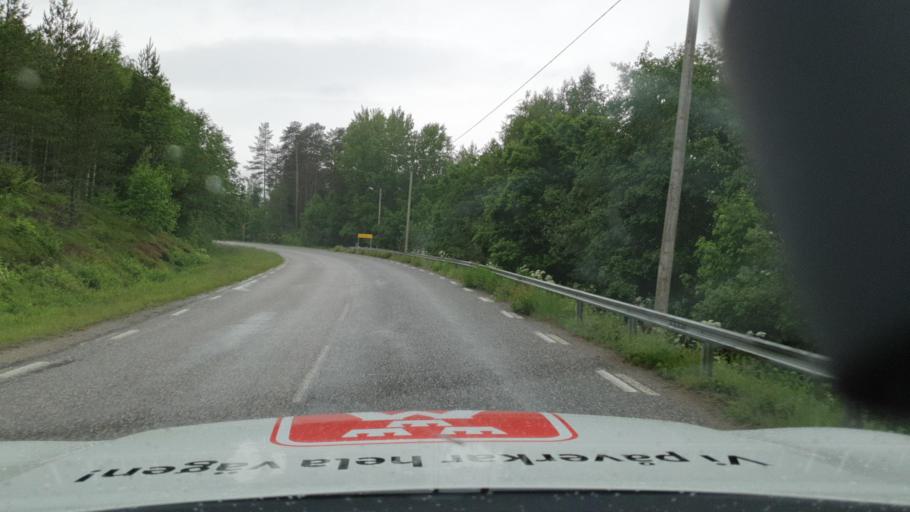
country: SE
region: Vaesterbotten
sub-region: Nordmalings Kommun
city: Nordmaling
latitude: 63.7973
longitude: 19.5175
